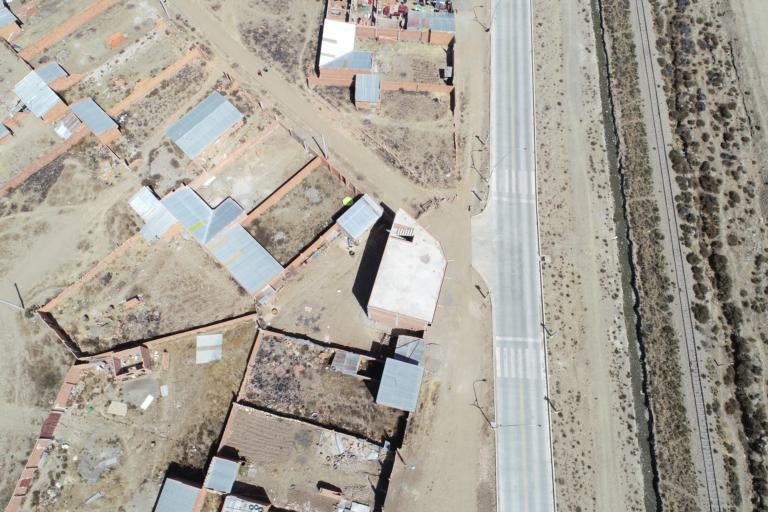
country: BO
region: La Paz
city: La Paz
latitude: -16.5920
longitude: -68.2137
